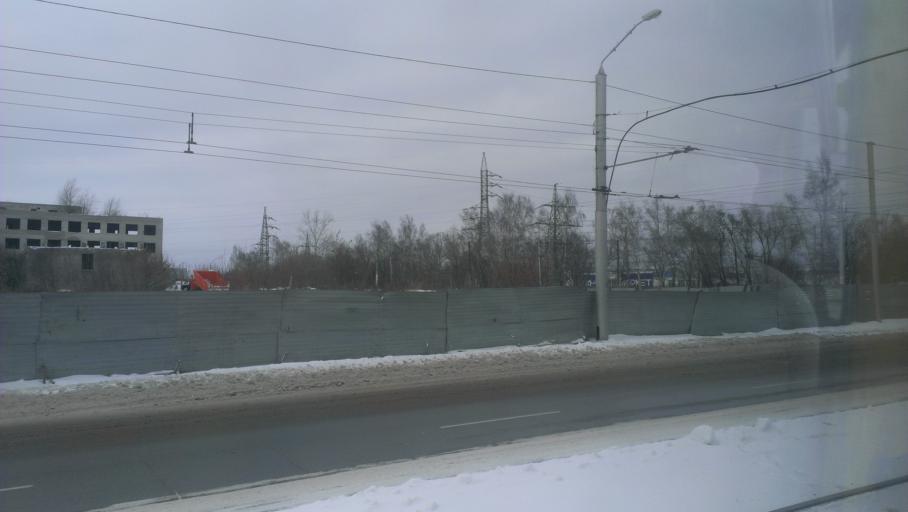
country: RU
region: Altai Krai
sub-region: Gorod Barnaulskiy
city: Barnaul
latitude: 53.3855
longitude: 83.7130
